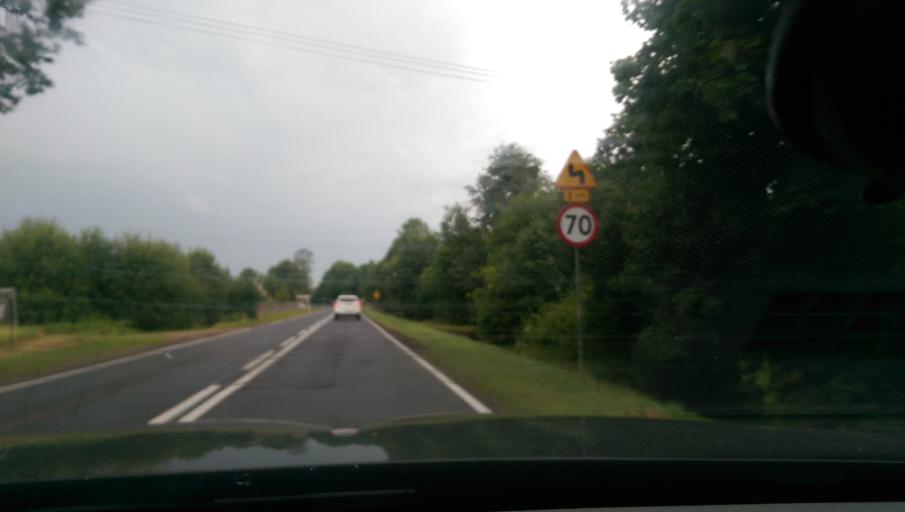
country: PL
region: Warmian-Masurian Voivodeship
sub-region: Powiat szczycienski
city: Szczytno
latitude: 53.5478
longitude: 20.9887
